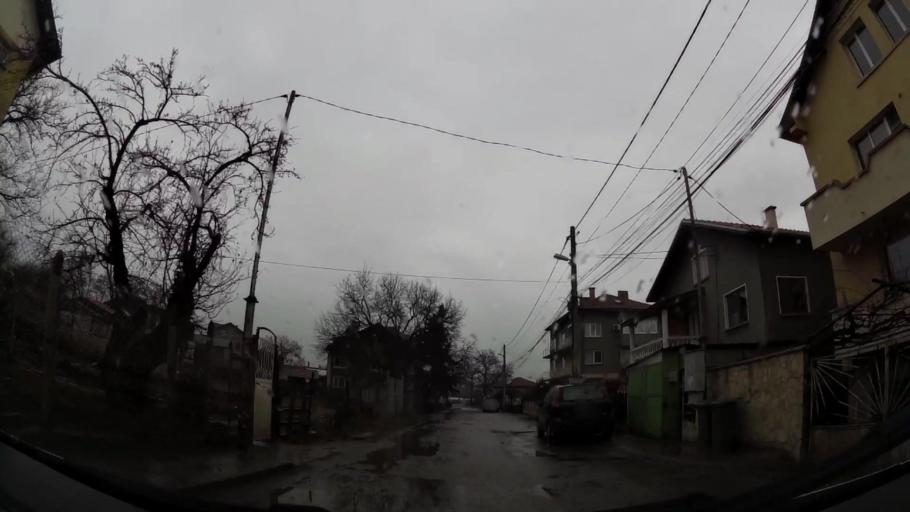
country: BG
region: Sofia-Capital
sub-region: Stolichna Obshtina
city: Sofia
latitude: 42.6296
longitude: 23.4051
